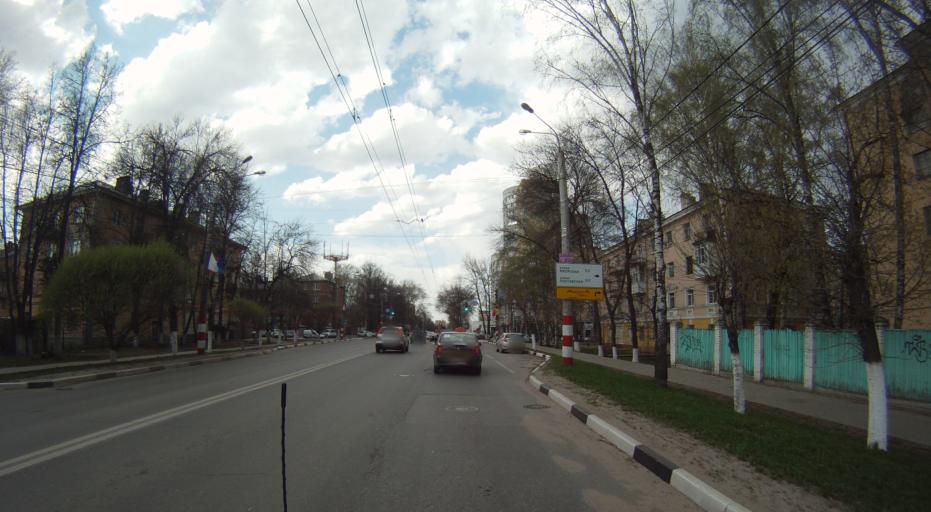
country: RU
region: Nizjnij Novgorod
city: Nizhniy Novgorod
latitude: 56.3126
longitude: 44.0194
